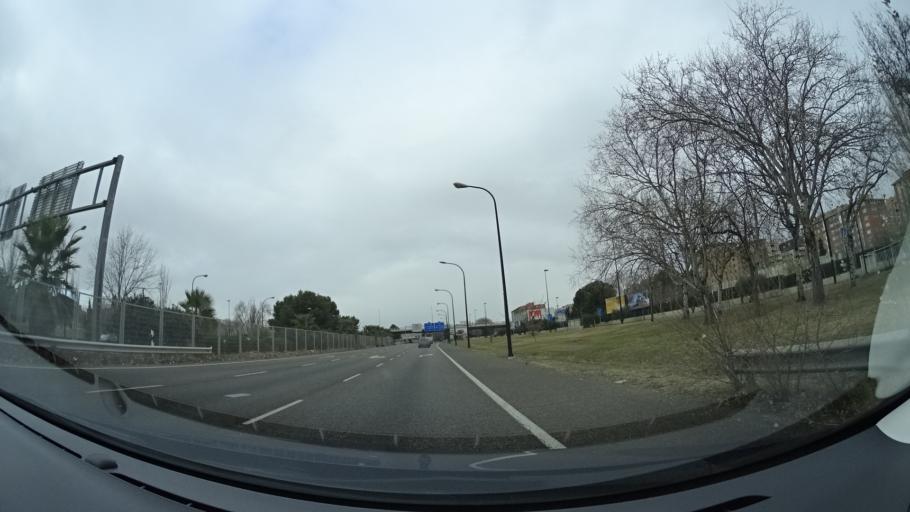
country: ES
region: Aragon
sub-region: Provincia de Zaragoza
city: Zaragoza
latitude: 41.6707
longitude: -0.8803
